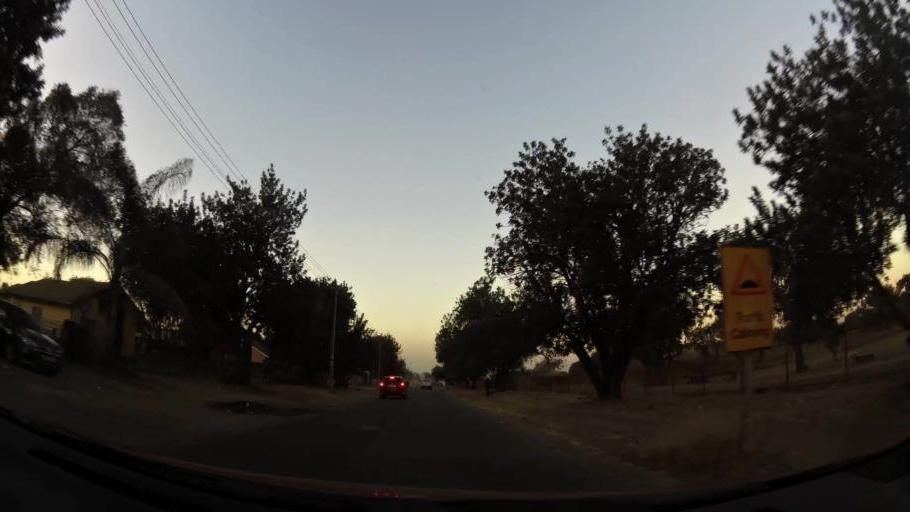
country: ZA
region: North-West
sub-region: Bojanala Platinum District Municipality
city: Rustenburg
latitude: -25.6563
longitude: 27.2388
